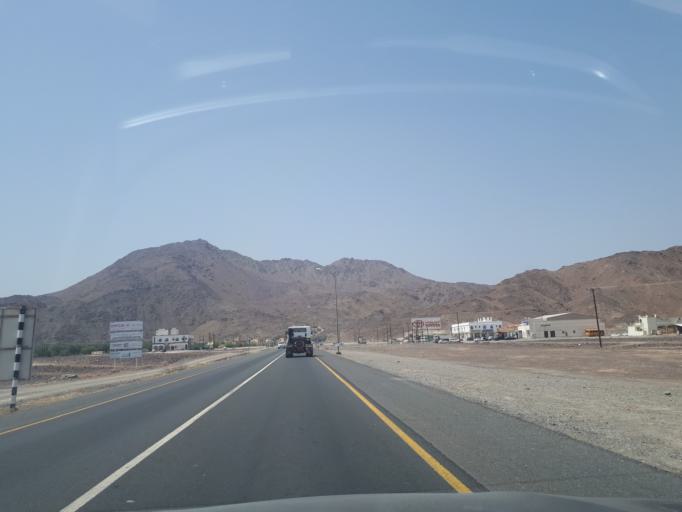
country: OM
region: Muhafazat ad Dakhiliyah
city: Sufalat Sama'il
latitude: 23.2576
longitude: 58.1030
